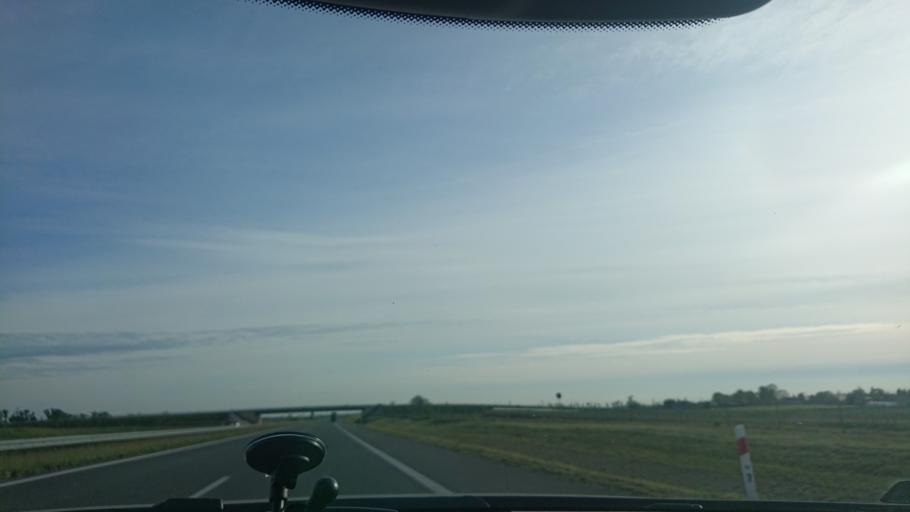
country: PL
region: Greater Poland Voivodeship
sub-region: Powiat gnieznienski
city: Gniezno
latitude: 52.5408
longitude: 17.5264
